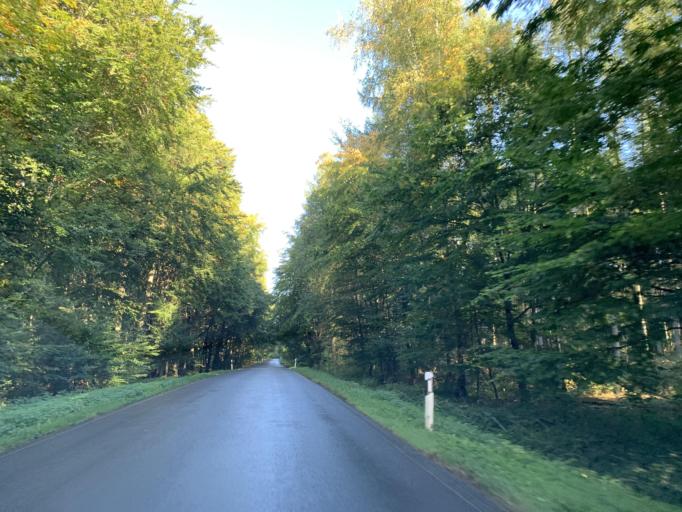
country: DE
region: Mecklenburg-Vorpommern
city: Burg Stargard
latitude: 53.4997
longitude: 13.2645
